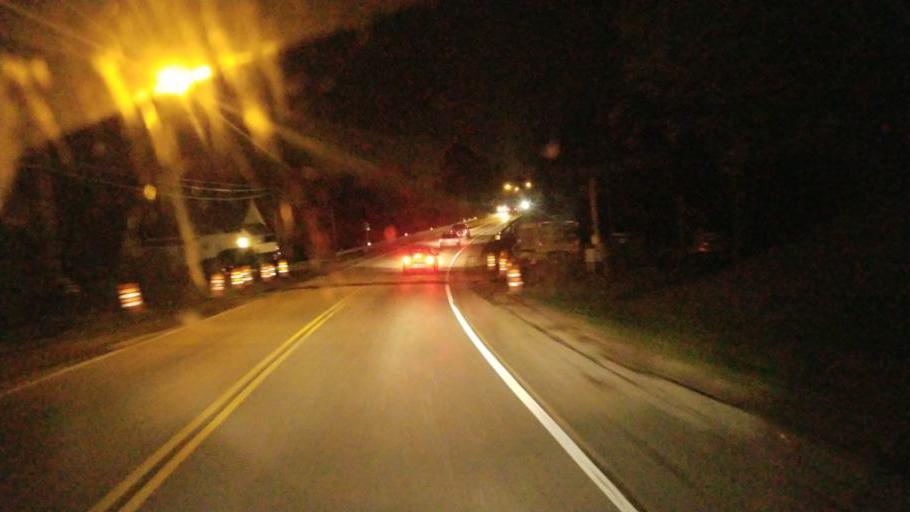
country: US
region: Ohio
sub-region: Wayne County
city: Apple Creek
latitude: 40.7443
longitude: -81.8306
